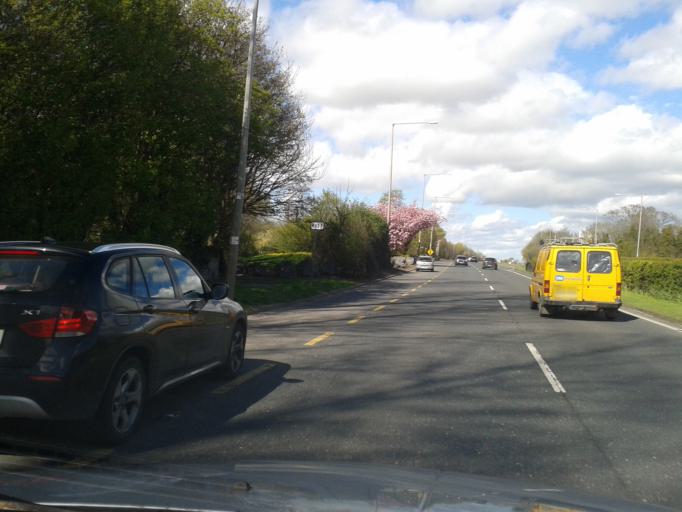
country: IE
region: Leinster
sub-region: Fingal County
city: Swords
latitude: 53.4697
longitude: -6.2127
